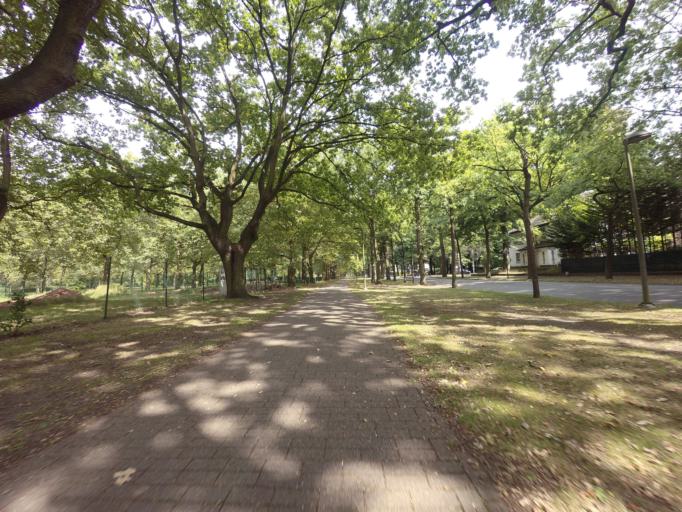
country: BE
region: Flanders
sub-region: Provincie Antwerpen
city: Antwerpen
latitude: 51.1844
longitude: 4.3988
